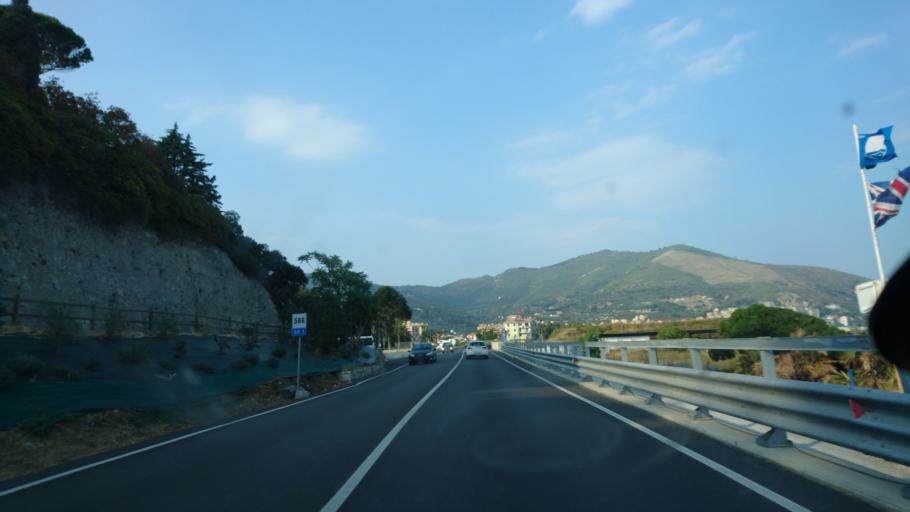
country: IT
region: Liguria
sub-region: Provincia di Savona
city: Spotorno
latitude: 44.2178
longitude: 8.4149
